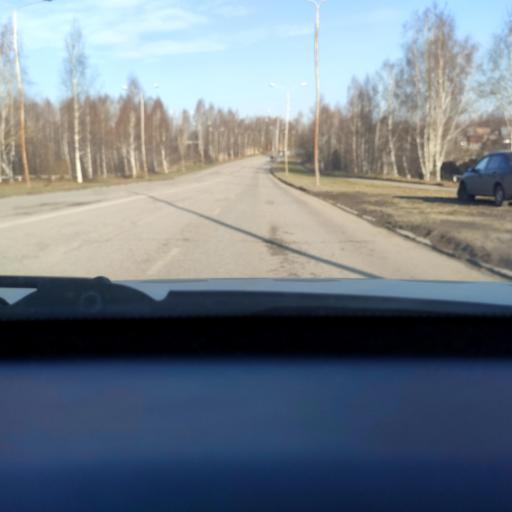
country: RU
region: Perm
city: Perm
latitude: 58.0957
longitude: 56.3847
